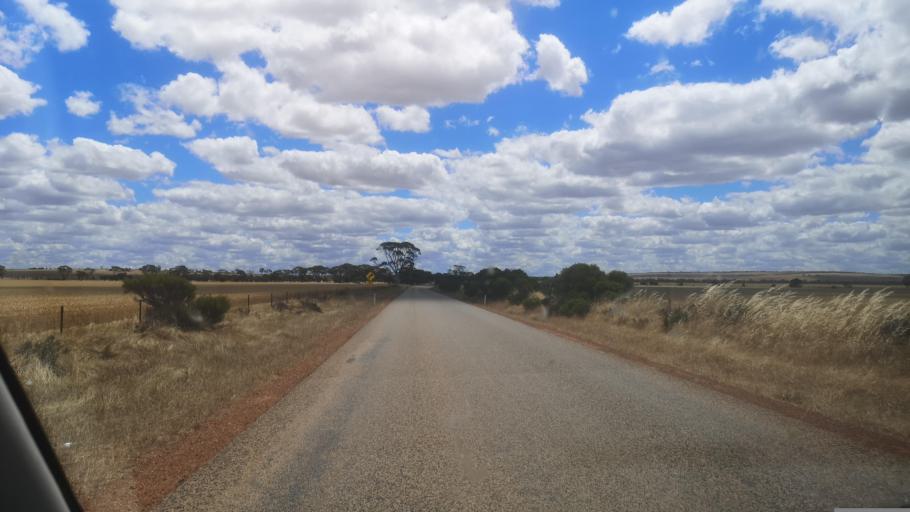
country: AU
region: Western Australia
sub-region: Cunderdin
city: Cunderdin
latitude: -32.0801
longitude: 117.4474
